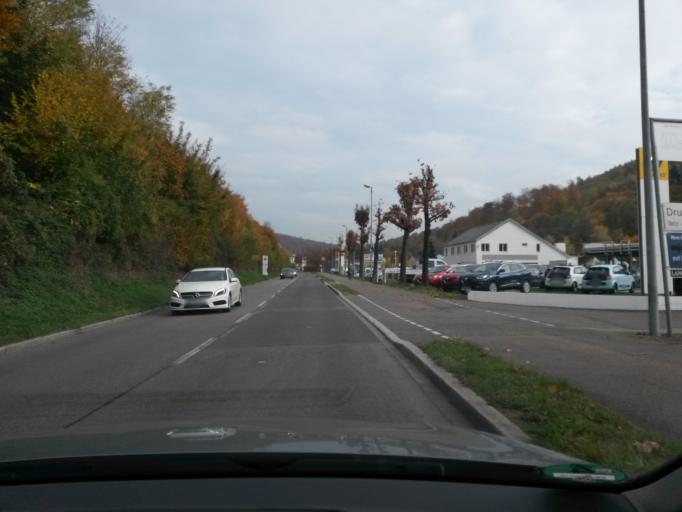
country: DE
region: Baden-Wuerttemberg
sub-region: Karlsruhe Region
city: Ettlingen
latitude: 48.9359
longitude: 8.4251
